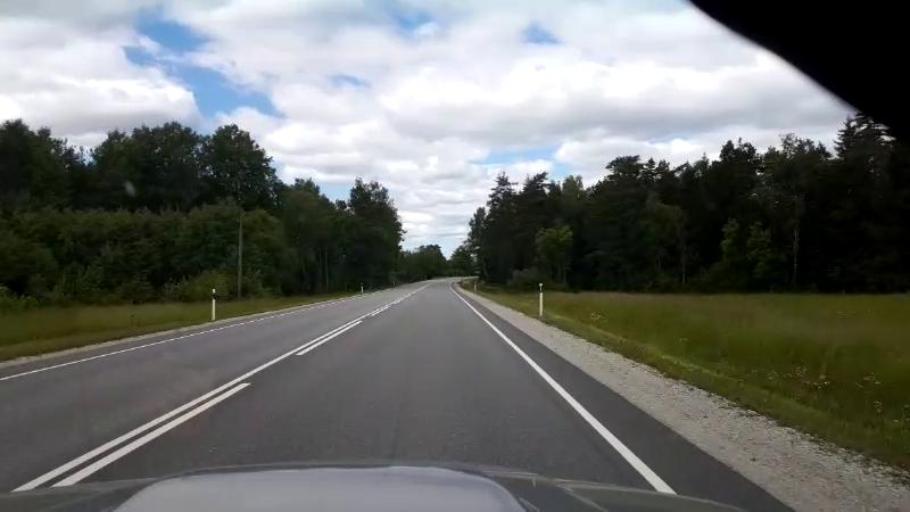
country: EE
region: Raplamaa
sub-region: Maerjamaa vald
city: Marjamaa
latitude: 58.9689
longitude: 24.4762
